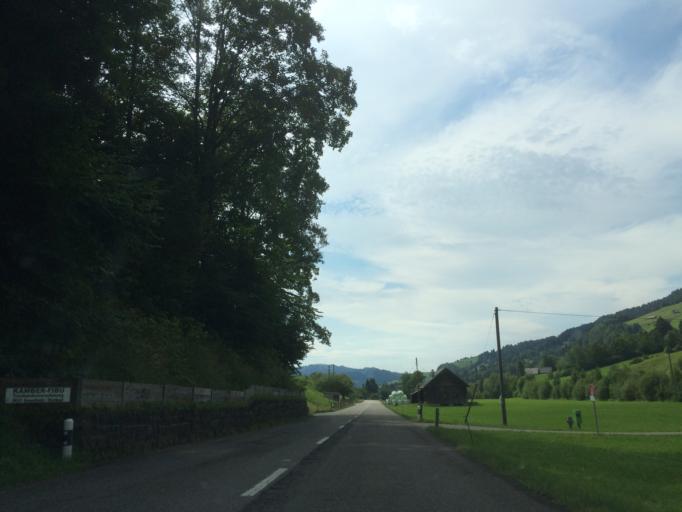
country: CH
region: Saint Gallen
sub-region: Wahlkreis Toggenburg
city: Krummenau
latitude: 47.2454
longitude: 9.2486
